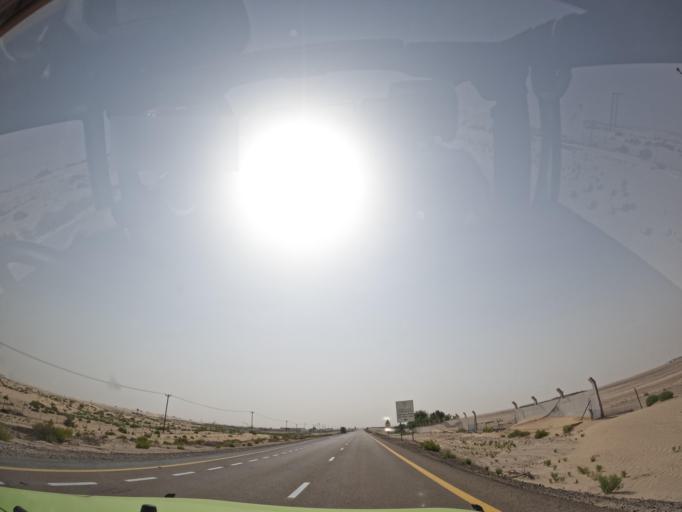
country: AE
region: Dubai
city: Dubai
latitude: 24.6677
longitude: 55.1734
